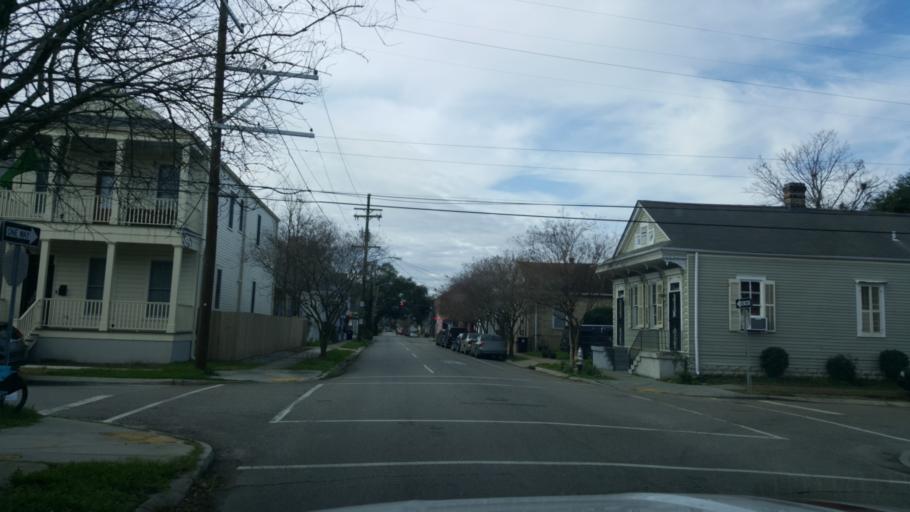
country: US
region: Louisiana
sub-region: Orleans Parish
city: New Orleans
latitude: 29.9718
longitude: -90.0750
